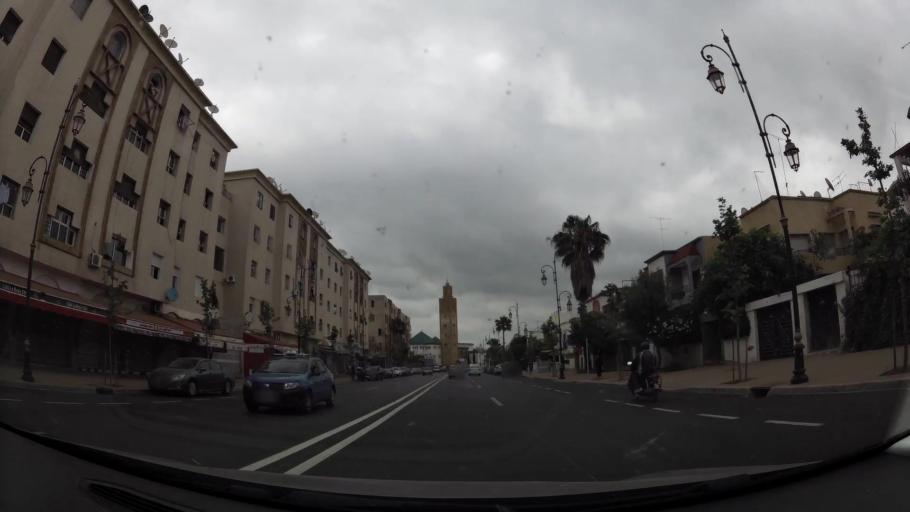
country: MA
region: Rabat-Sale-Zemmour-Zaer
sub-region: Rabat
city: Rabat
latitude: 33.9793
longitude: -6.8138
